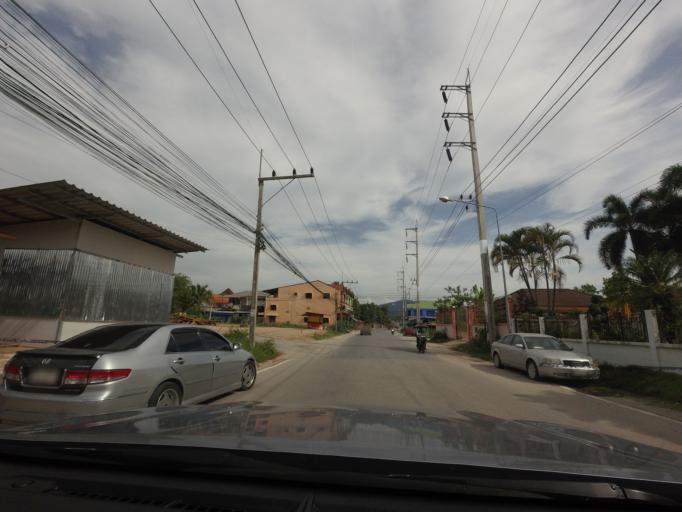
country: TH
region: Yala
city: Yala
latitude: 6.5324
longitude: 101.2928
